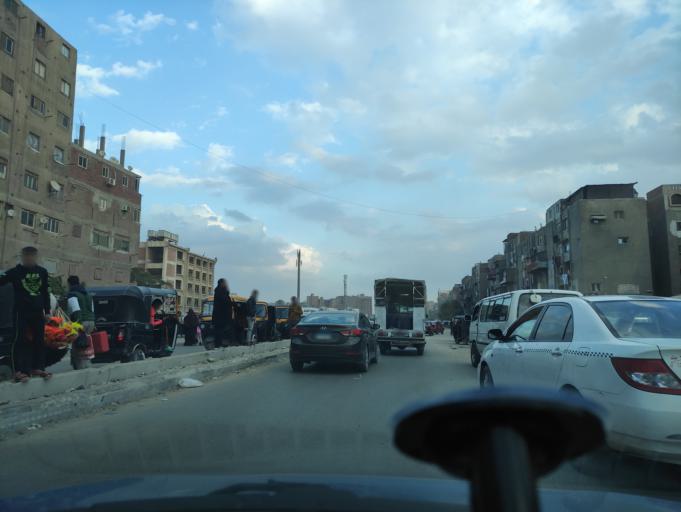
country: EG
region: Muhafazat al Qalyubiyah
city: Al Khankah
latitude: 30.1369
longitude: 31.3504
